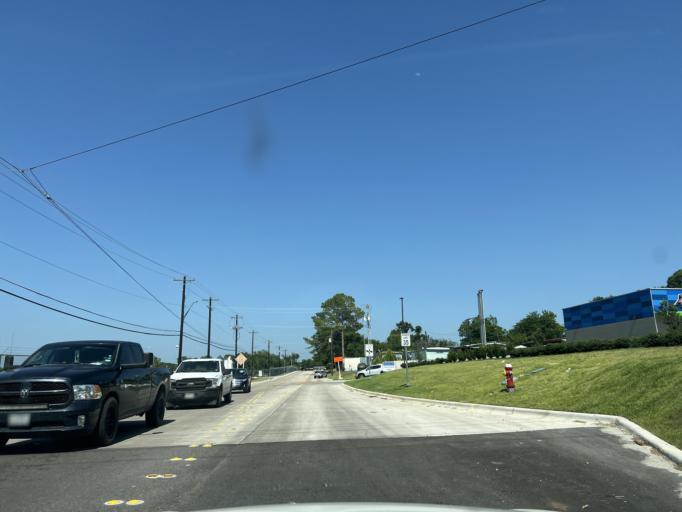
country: US
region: Texas
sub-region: Washington County
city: Brenham
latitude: 30.1700
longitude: -96.3813
